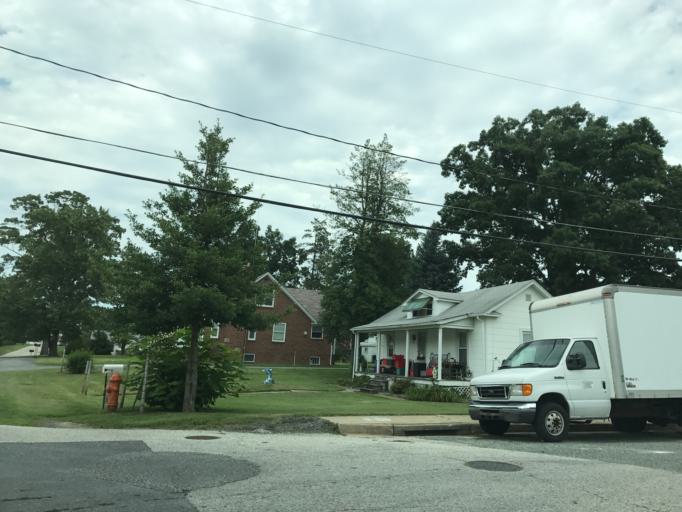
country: US
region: Maryland
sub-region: Baltimore County
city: Essex
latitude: 39.3131
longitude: -76.4851
